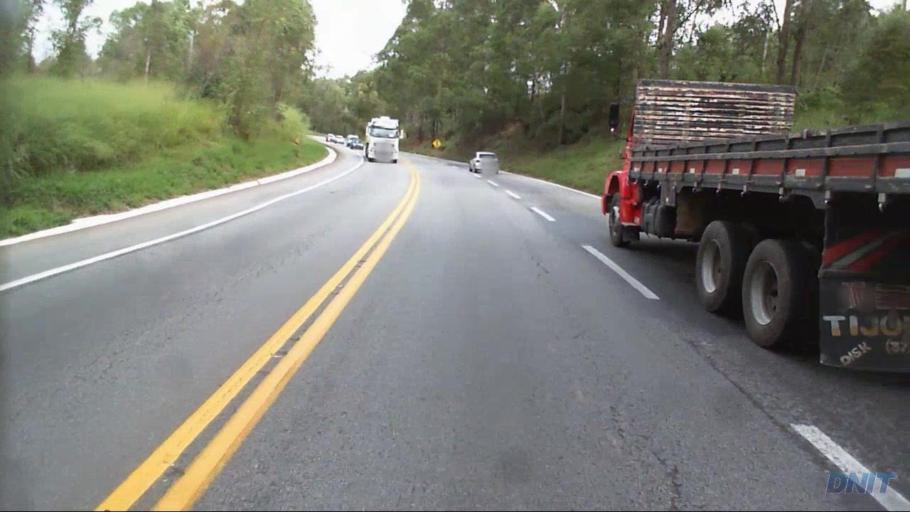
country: BR
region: Minas Gerais
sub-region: Caete
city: Caete
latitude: -19.7287
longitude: -43.5943
